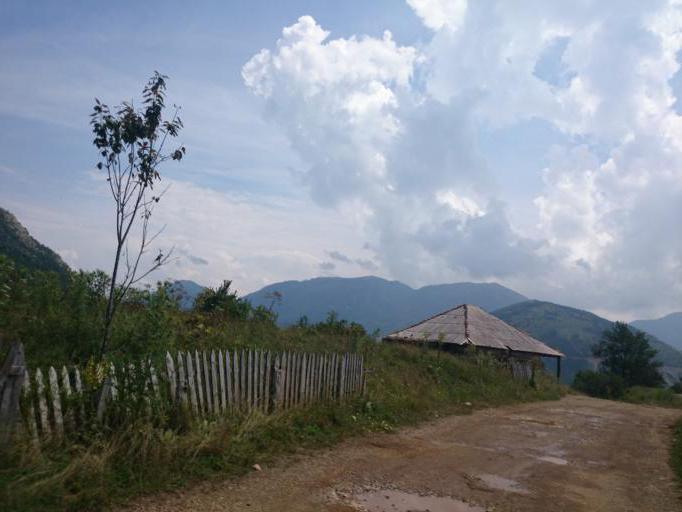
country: AL
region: Diber
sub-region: Rrethi i Dibres
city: Fushe-Lure
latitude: 41.8364
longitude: 20.1767
